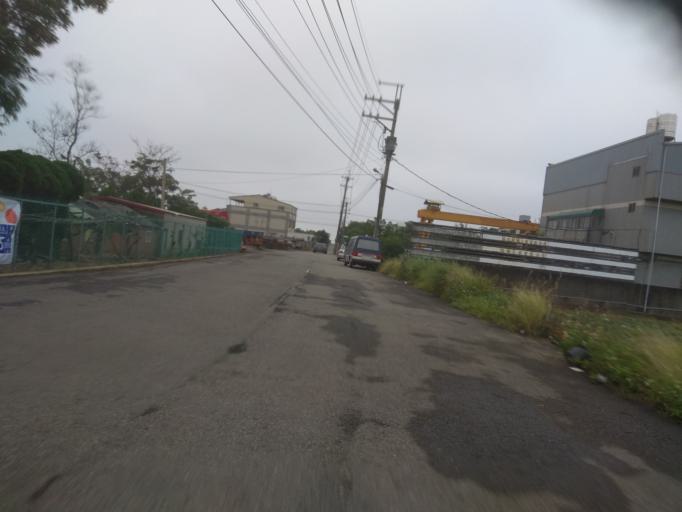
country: TW
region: Taiwan
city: Taoyuan City
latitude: 24.9954
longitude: 121.1242
